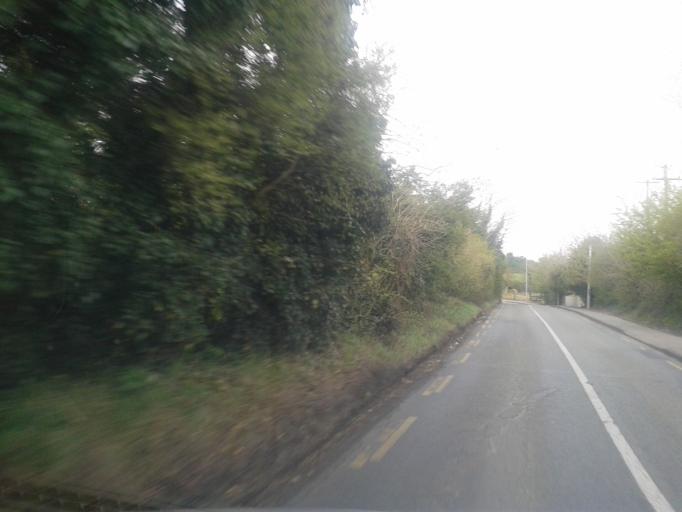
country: IE
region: Leinster
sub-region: Fingal County
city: Swords
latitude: 53.4583
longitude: -6.2565
